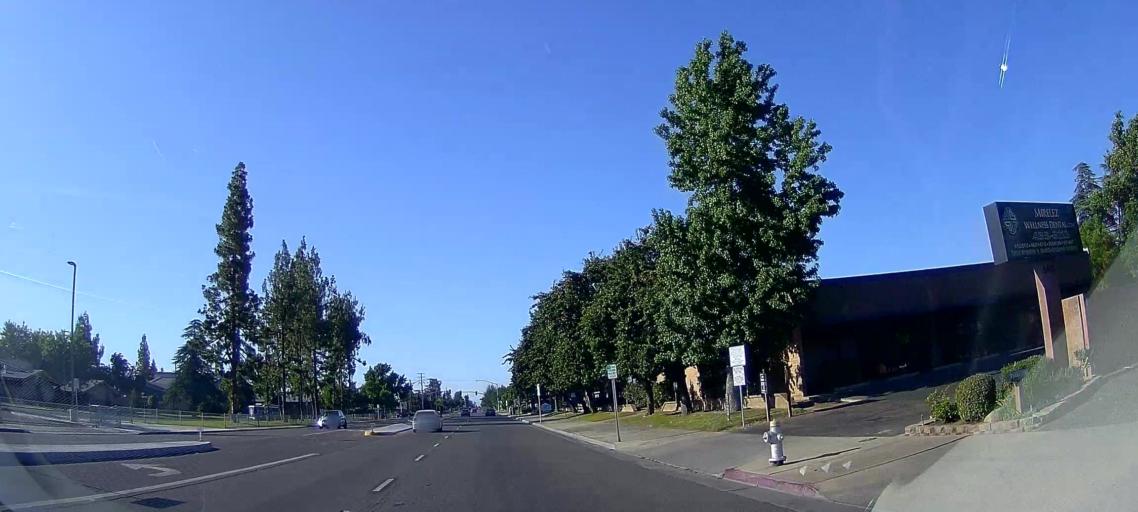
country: US
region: California
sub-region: Fresno County
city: Fresno
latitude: 36.8173
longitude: -119.8083
